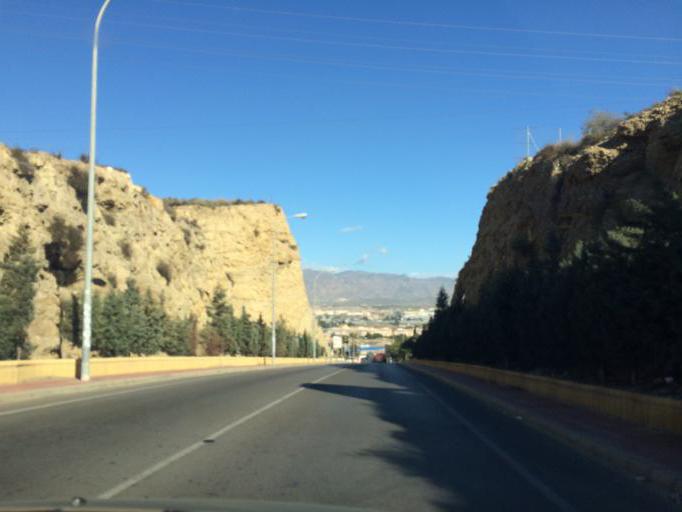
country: ES
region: Andalusia
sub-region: Provincia de Almeria
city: Huercal de Almeria
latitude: 36.8641
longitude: -2.4436
